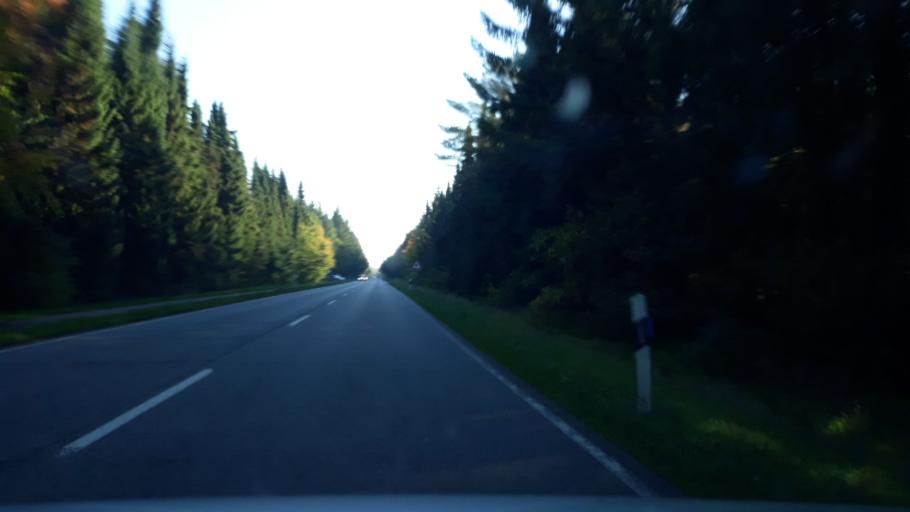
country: DE
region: Schleswig-Holstein
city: Kropp
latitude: 54.4029
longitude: 9.4962
